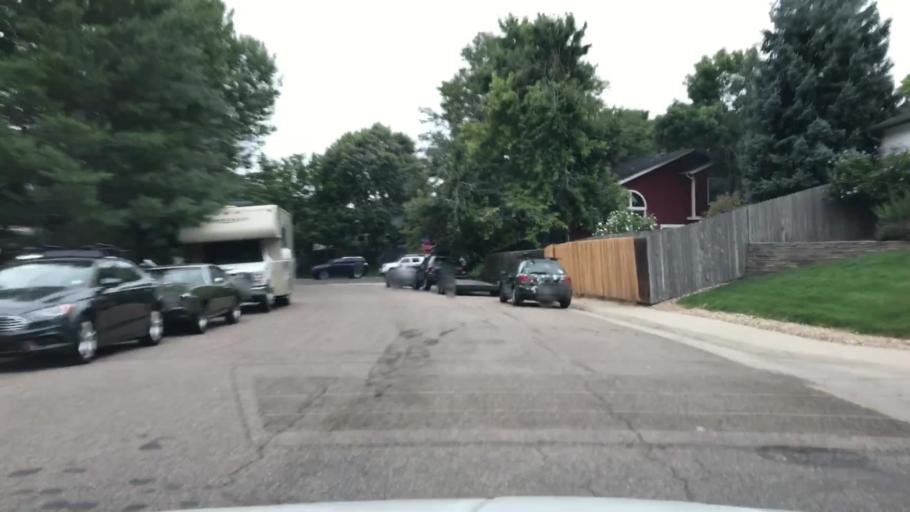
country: US
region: Colorado
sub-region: Broomfield County
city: Broomfield
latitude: 39.9263
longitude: -105.0394
